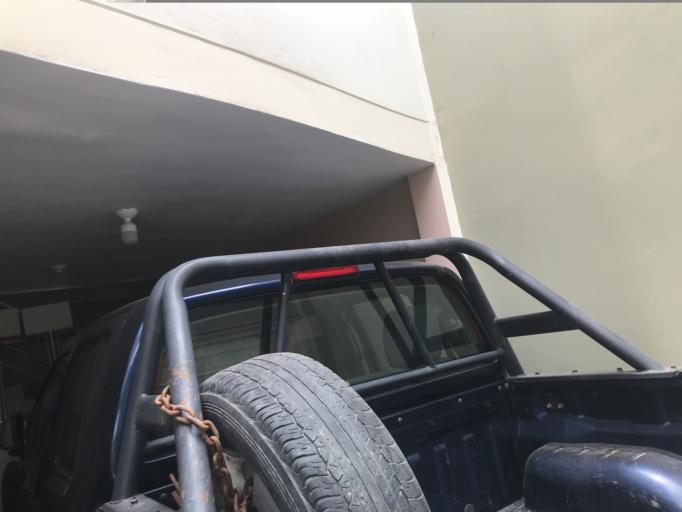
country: PE
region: Lambayeque
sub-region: Provincia de Chiclayo
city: Chiclayo
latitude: -6.7708
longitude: -79.8564
